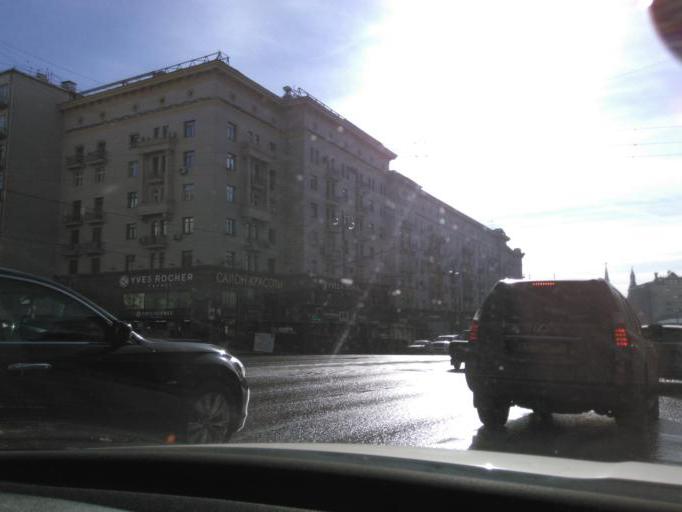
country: RU
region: Moscow
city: Moscow
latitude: 55.7593
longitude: 37.6116
